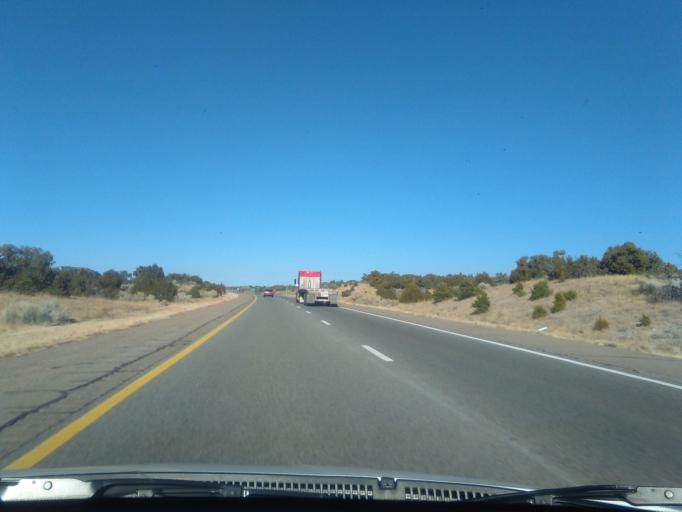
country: US
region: New Mexico
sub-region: Santa Fe County
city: Eldorado at Santa Fe
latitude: 35.5708
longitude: -105.8893
